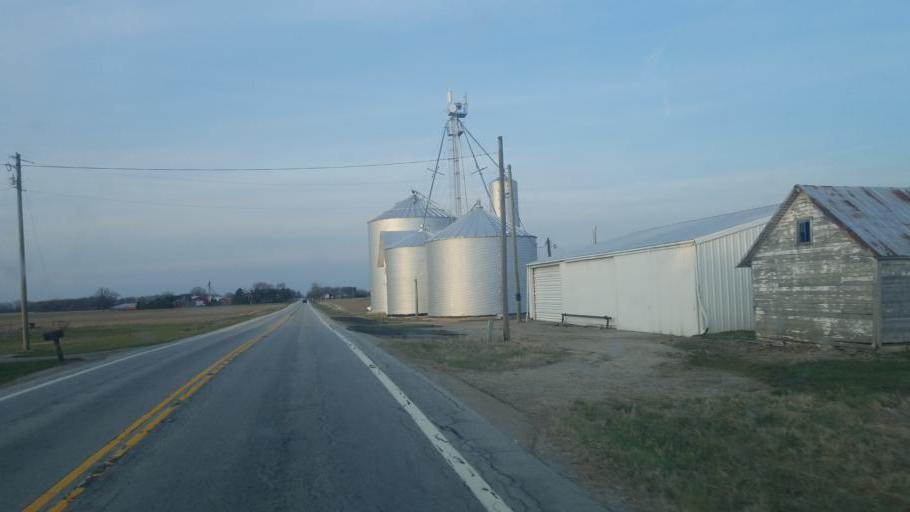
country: US
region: Ohio
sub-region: Union County
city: Richwood
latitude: 40.3772
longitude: -83.2832
